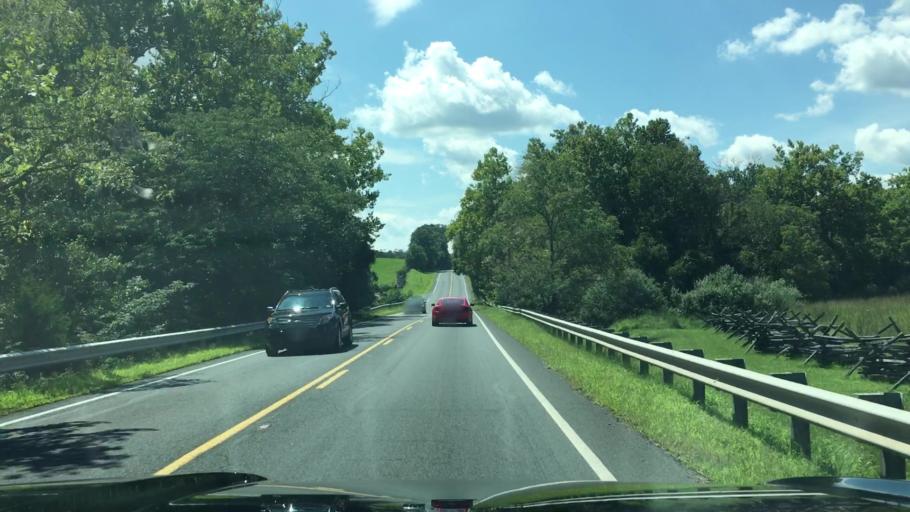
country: US
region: Virginia
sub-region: Prince William County
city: Bull Run
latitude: 38.8143
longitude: -77.5430
